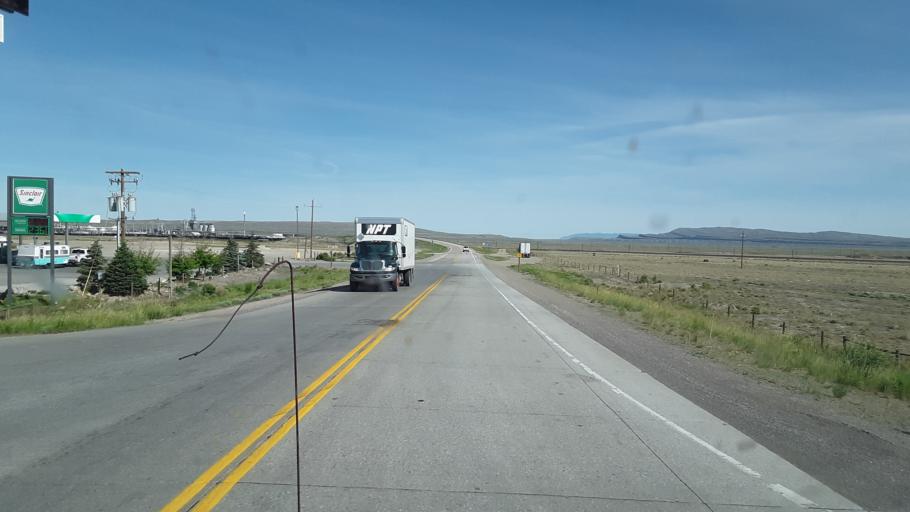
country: US
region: Wyoming
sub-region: Carbon County
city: Rawlins
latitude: 41.7732
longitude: -107.0829
